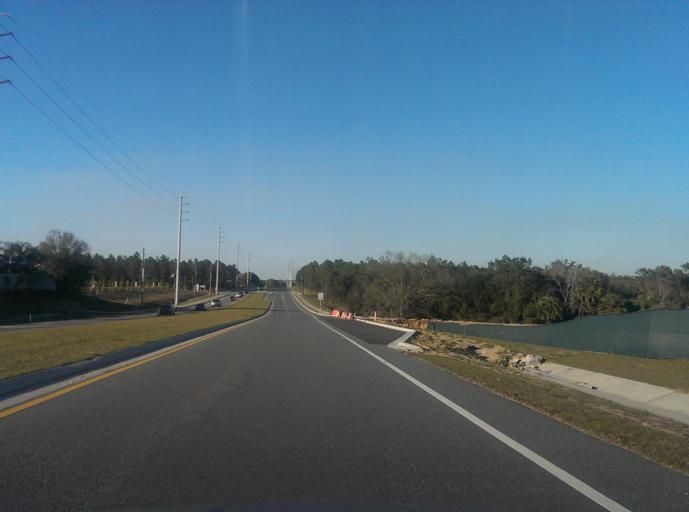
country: US
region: Florida
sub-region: Polk County
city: Loughman
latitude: 28.2929
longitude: -81.5906
